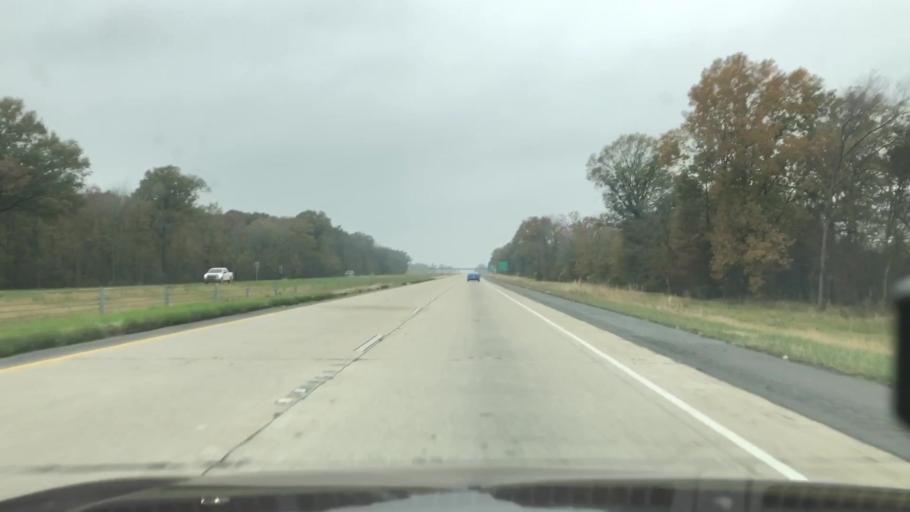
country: US
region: Louisiana
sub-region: Ouachita Parish
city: Lakeshore
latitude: 32.4882
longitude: -91.9795
